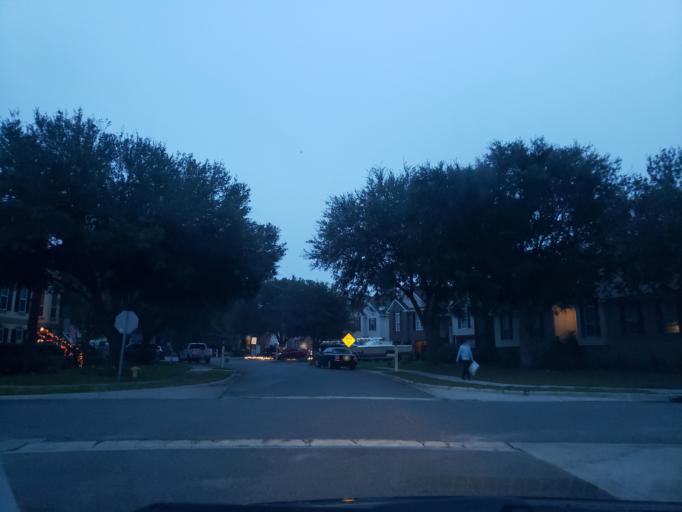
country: US
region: Georgia
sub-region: Chatham County
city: Wilmington Island
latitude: 32.0243
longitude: -80.9577
